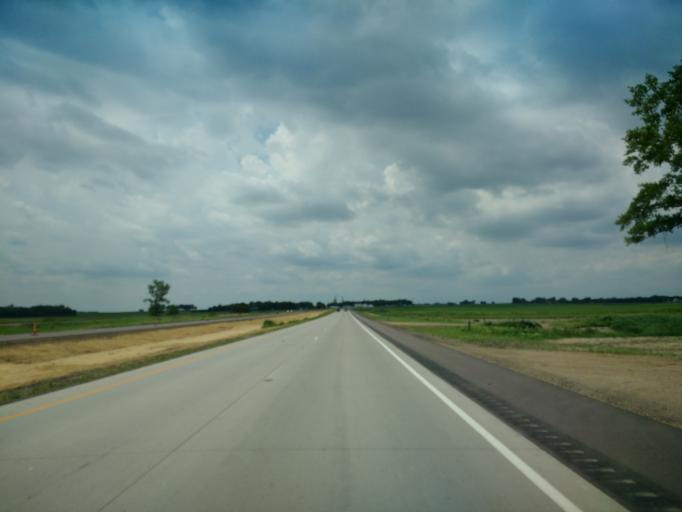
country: US
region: Minnesota
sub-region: Cottonwood County
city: Mountain Lake
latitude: 43.9136
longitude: -95.0190
